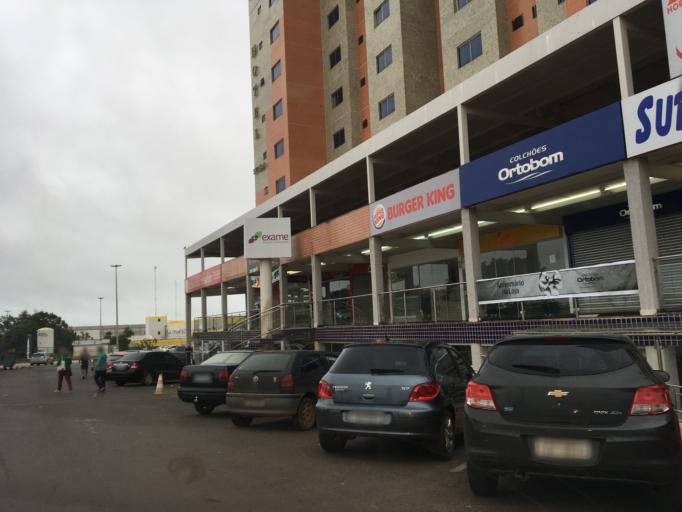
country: BR
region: Goias
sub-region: Luziania
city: Luziania
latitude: -16.0215
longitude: -48.0675
